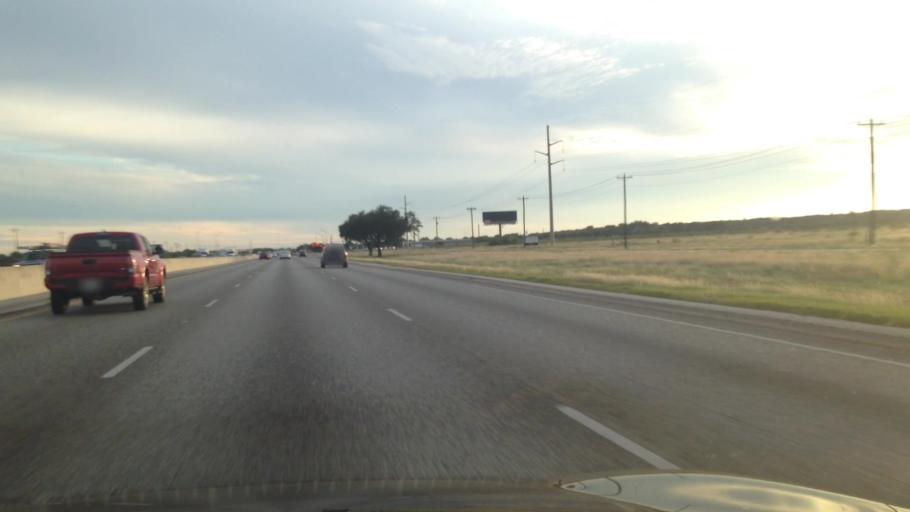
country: US
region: Texas
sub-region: Hays County
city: Kyle
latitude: 29.9295
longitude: -97.8894
